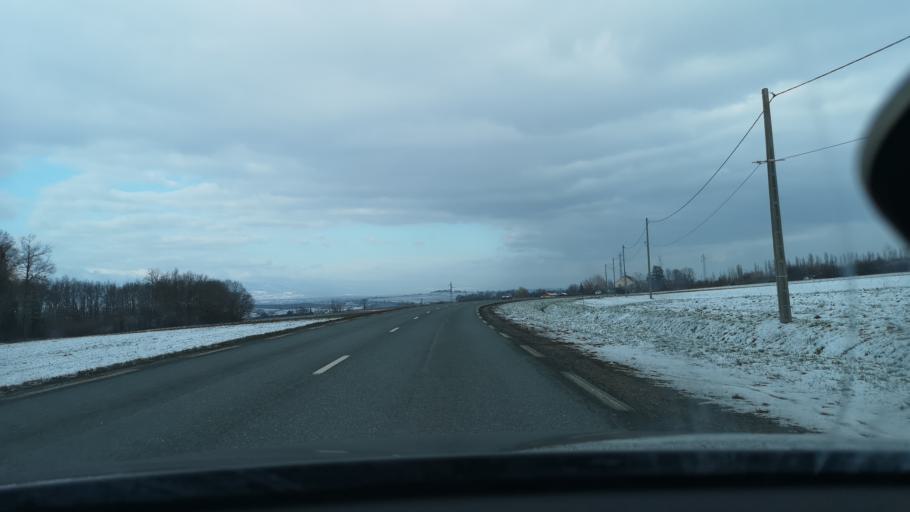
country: FR
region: Rhone-Alpes
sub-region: Departement de la Haute-Savoie
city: Viry
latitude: 46.1271
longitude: 6.0433
